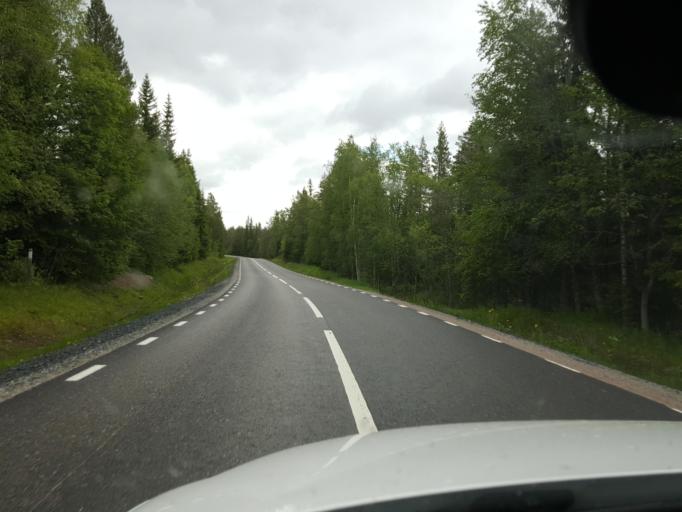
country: SE
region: Gaevleborg
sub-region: Ljusdals Kommun
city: Farila
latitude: 61.7558
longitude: 15.4244
